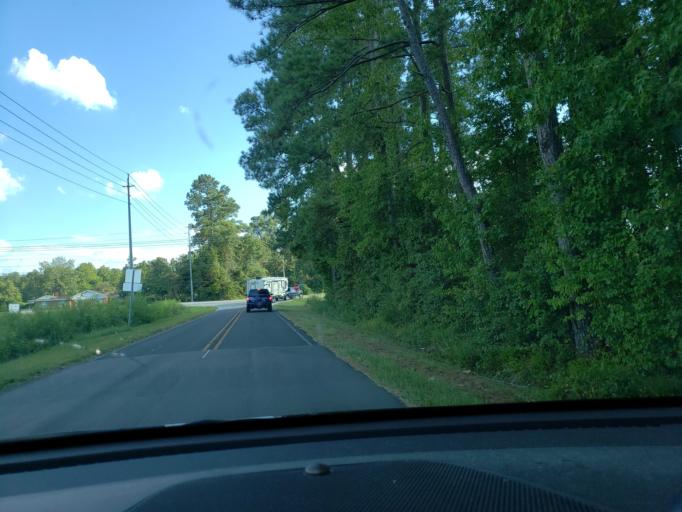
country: US
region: North Carolina
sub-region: Columbus County
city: Tabor City
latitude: 34.1601
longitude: -78.8511
